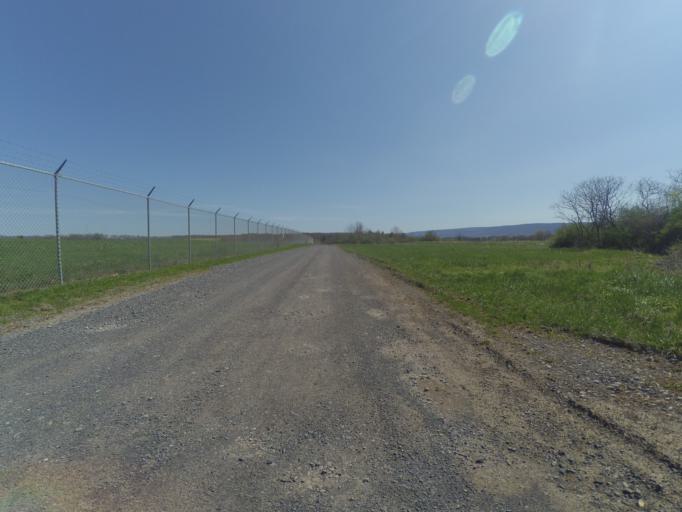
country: US
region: Pennsylvania
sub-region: Centre County
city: Houserville
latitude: 40.8538
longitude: -77.8372
